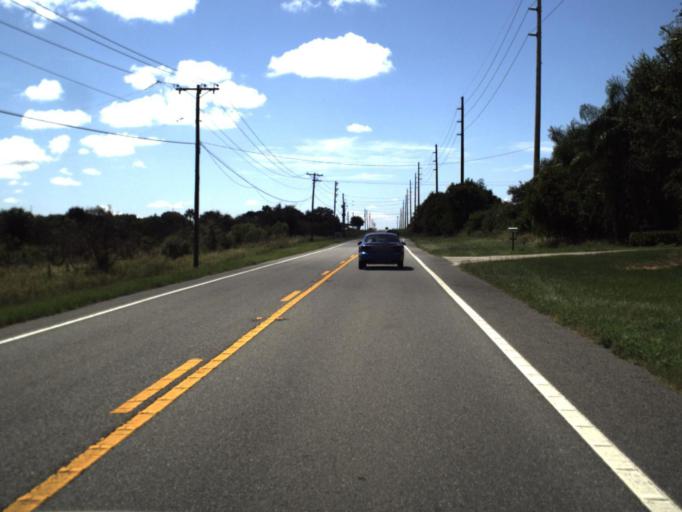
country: US
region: Florida
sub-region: Polk County
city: Dundee
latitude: 27.9922
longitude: -81.5950
